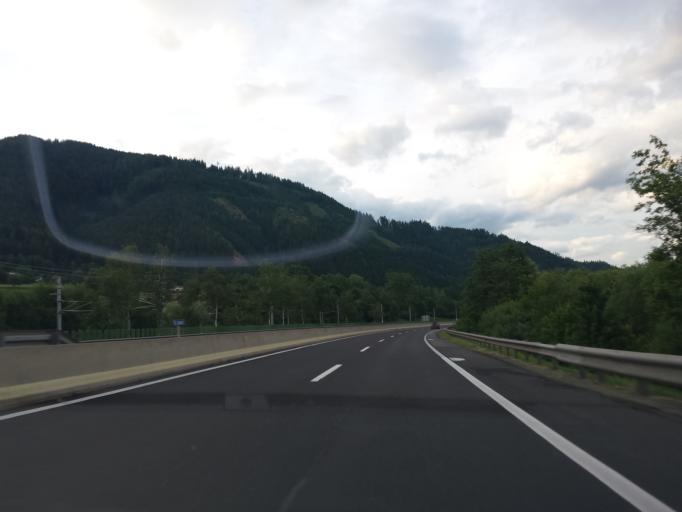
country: AT
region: Styria
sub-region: Politischer Bezirk Leoben
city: Kraubath an der Mur
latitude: 47.3128
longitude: 14.9518
